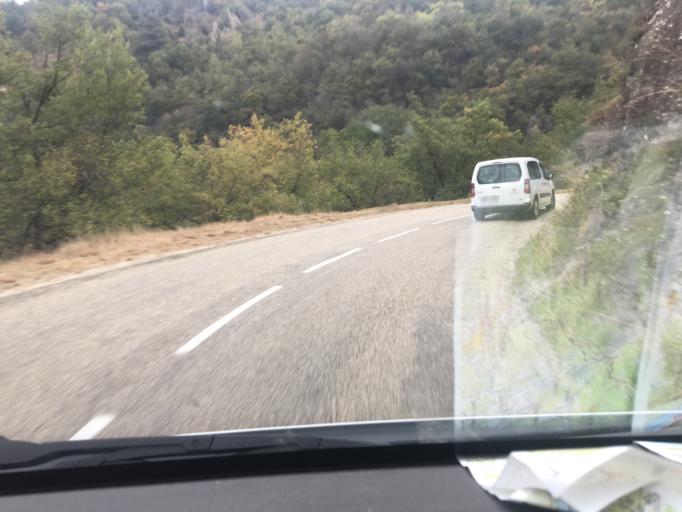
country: FR
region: Rhone-Alpes
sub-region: Departement de l'Ardeche
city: Saint-Jean-de-Muzols
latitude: 45.0587
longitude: 4.7469
